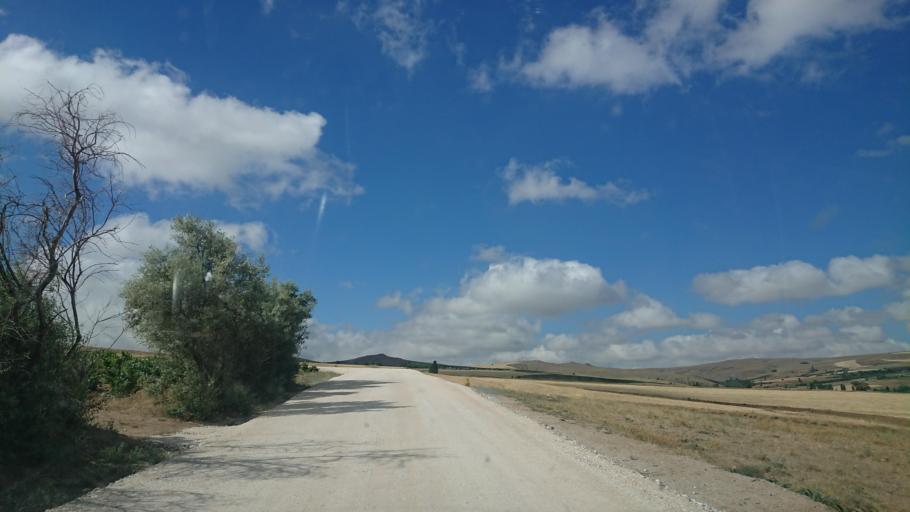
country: TR
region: Aksaray
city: Agacoren
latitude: 38.8544
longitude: 33.9404
